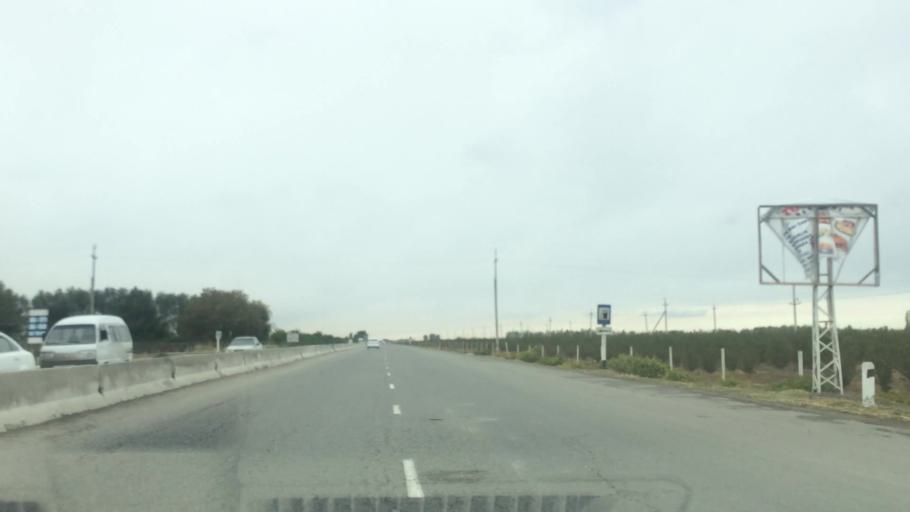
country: UZ
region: Samarqand
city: Bulung'ur
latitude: 39.7507
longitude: 67.2212
